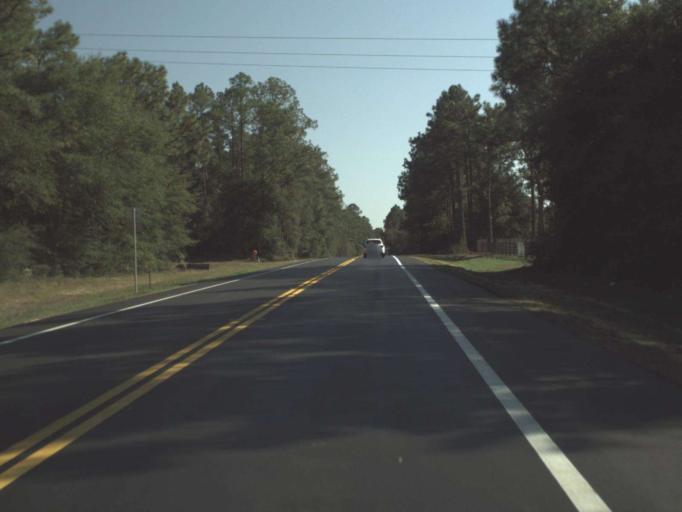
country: US
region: Florida
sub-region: Walton County
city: DeFuniak Springs
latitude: 30.7577
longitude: -86.1511
